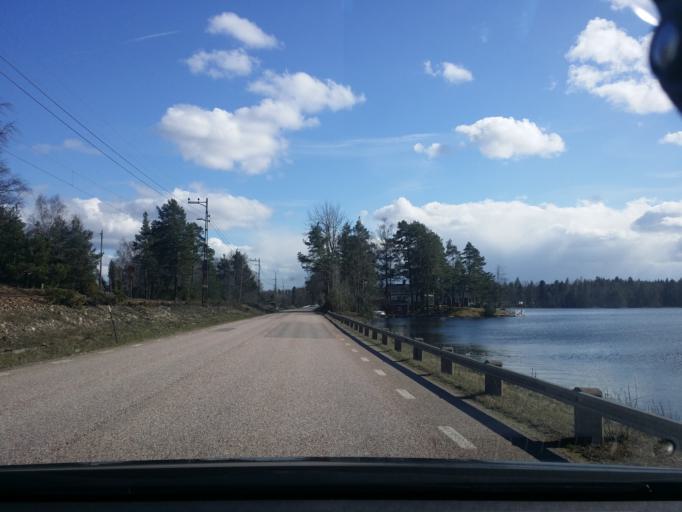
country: SE
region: Vaestmanland
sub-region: Sala Kommun
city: Sala
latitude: 59.9611
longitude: 16.5136
